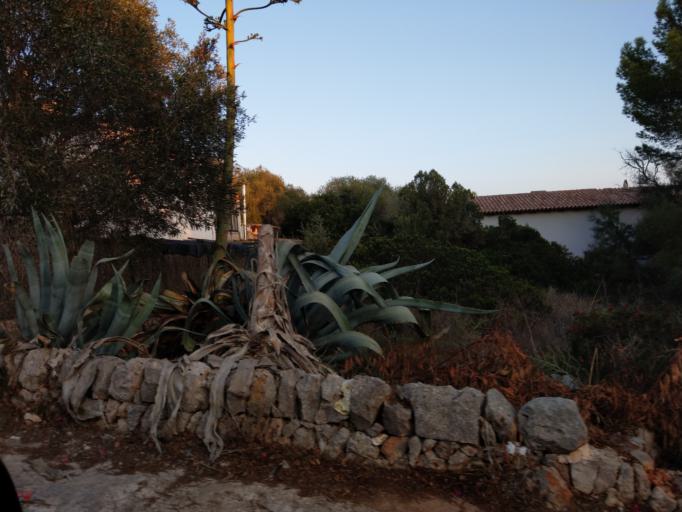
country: ES
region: Balearic Islands
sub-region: Illes Balears
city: Santanyi
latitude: 39.3141
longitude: 3.1187
